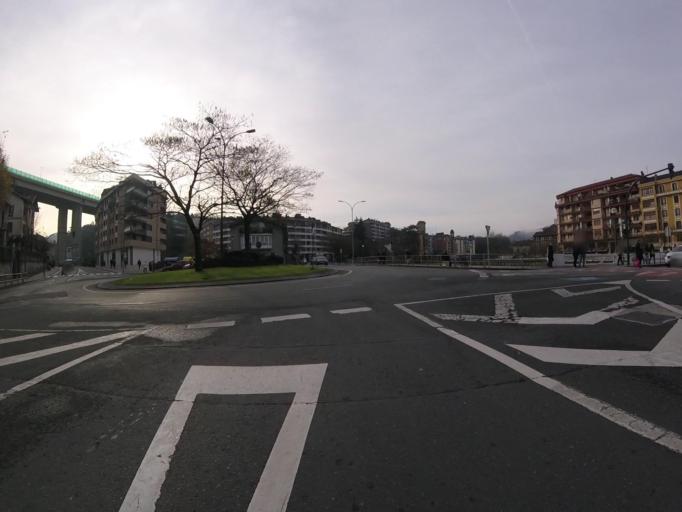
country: ES
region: Basque Country
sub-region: Provincia de Guipuzcoa
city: Tolosa
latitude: 43.1349
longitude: -2.0725
